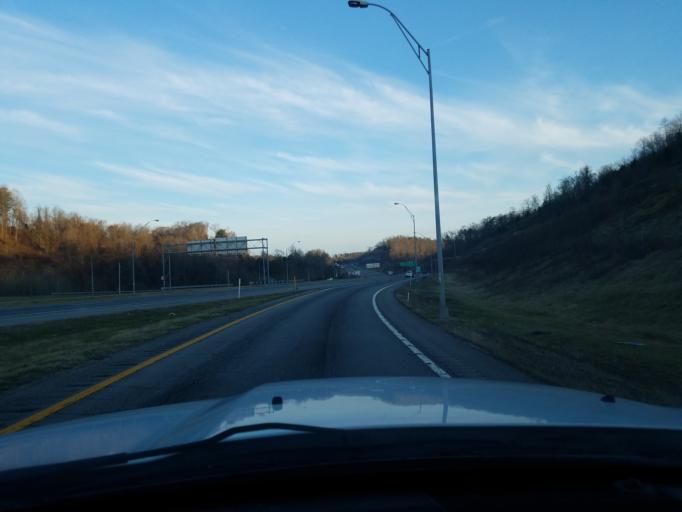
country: US
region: West Virginia
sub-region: Putnam County
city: Teays Valley
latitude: 38.4561
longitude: -81.9034
